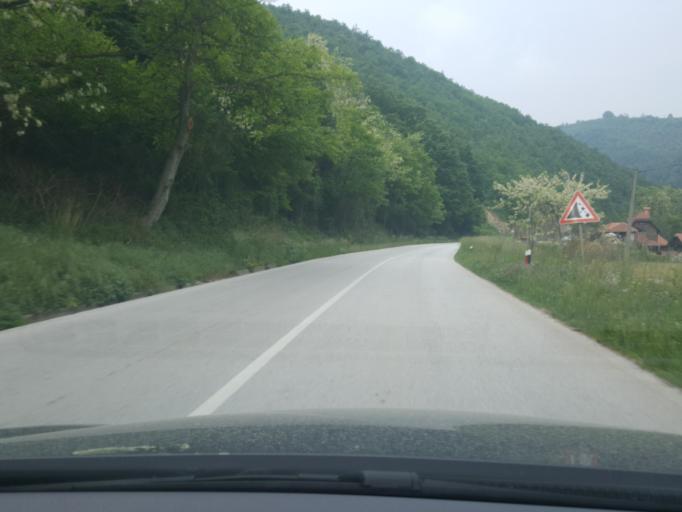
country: RS
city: Gornja Bukovica
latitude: 44.2540
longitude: 19.8012
